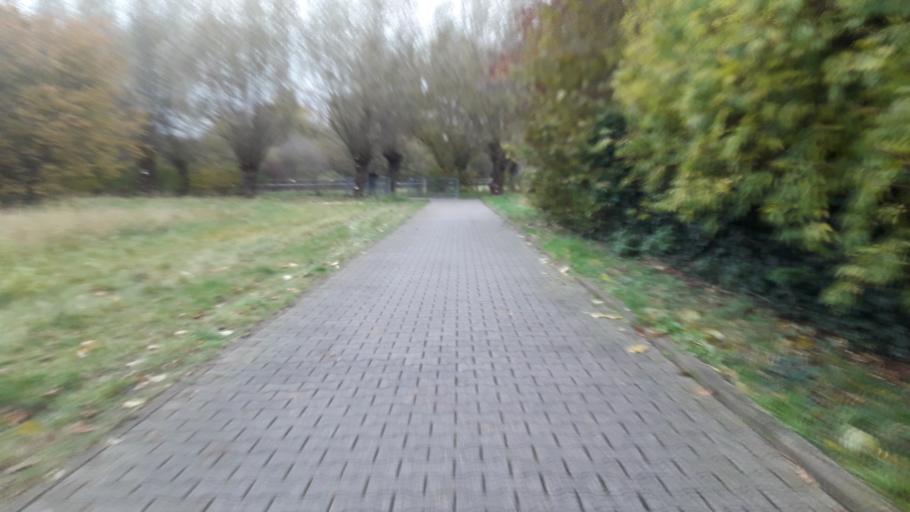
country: DE
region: North Rhine-Westphalia
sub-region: Regierungsbezirk Detmold
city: Paderborn
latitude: 51.7294
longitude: 8.7790
